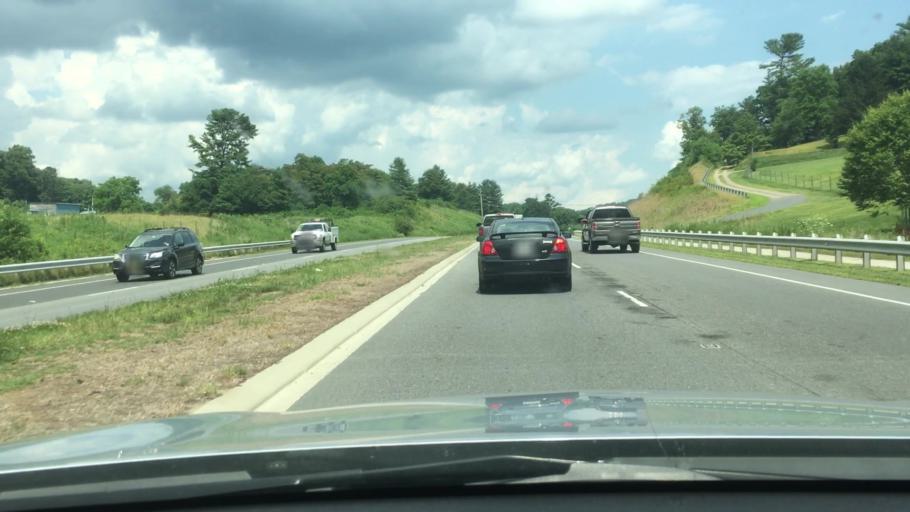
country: US
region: North Carolina
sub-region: Yancey County
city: Burnsville
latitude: 35.9126
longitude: -82.3268
